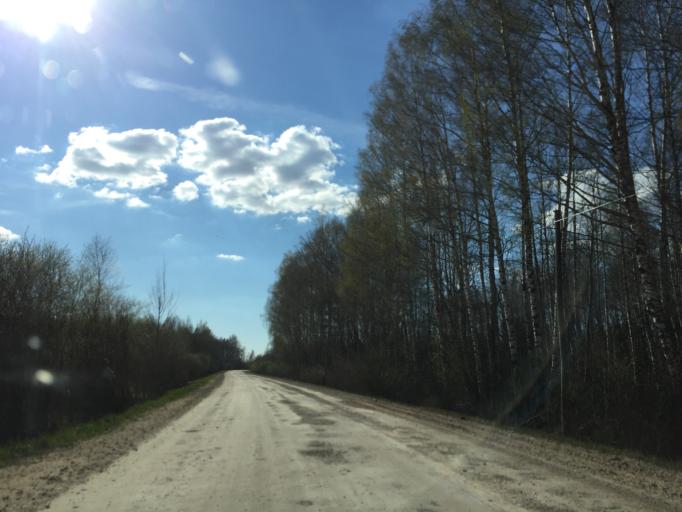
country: LV
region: Saulkrastu
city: Saulkrasti
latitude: 57.3460
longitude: 24.5917
